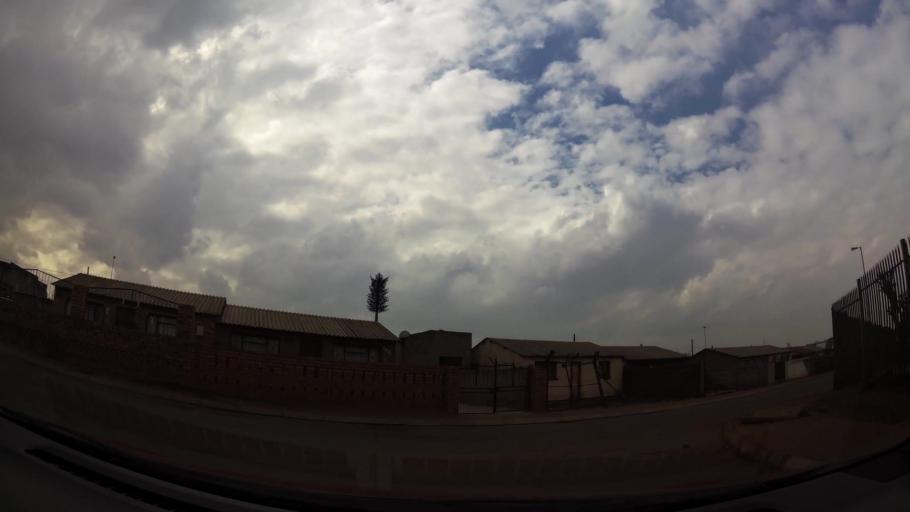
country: ZA
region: Gauteng
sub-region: City of Johannesburg Metropolitan Municipality
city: Soweto
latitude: -26.2557
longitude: 27.8302
